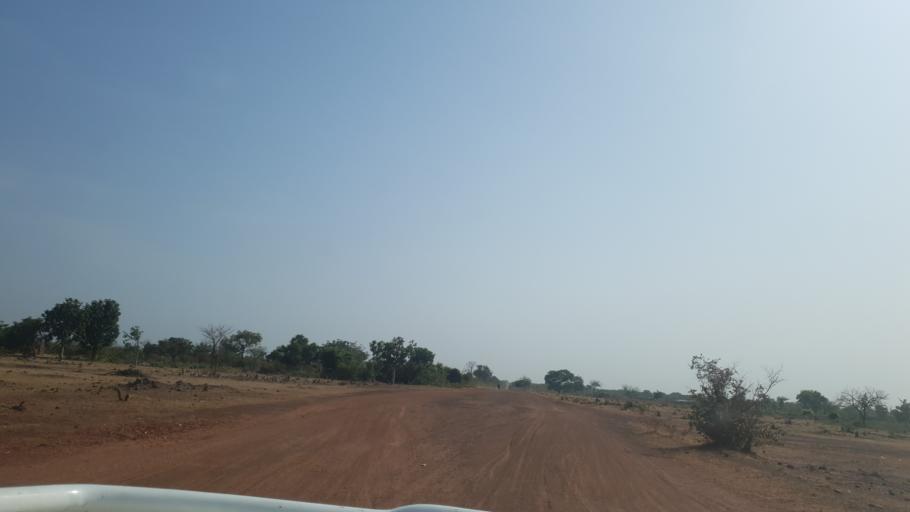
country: ML
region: Koulikoro
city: Dioila
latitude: 12.6678
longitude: -6.6931
